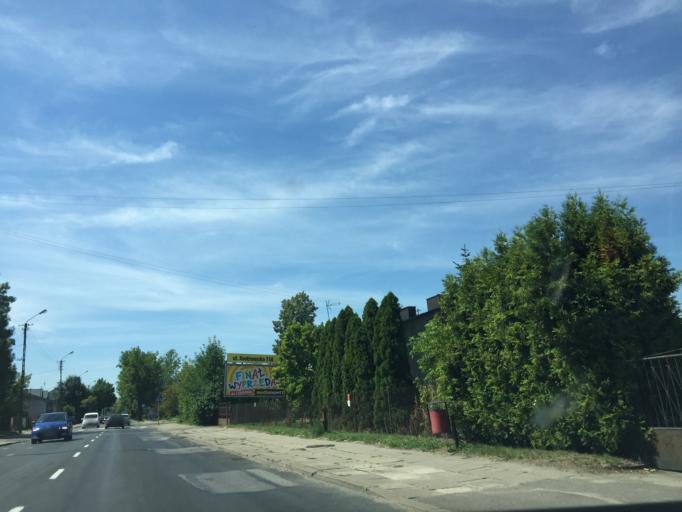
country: PL
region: Lodz Voivodeship
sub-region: Piotrkow Trybunalski
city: Piotrkow Trybunalski
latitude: 51.4126
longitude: 19.7083
